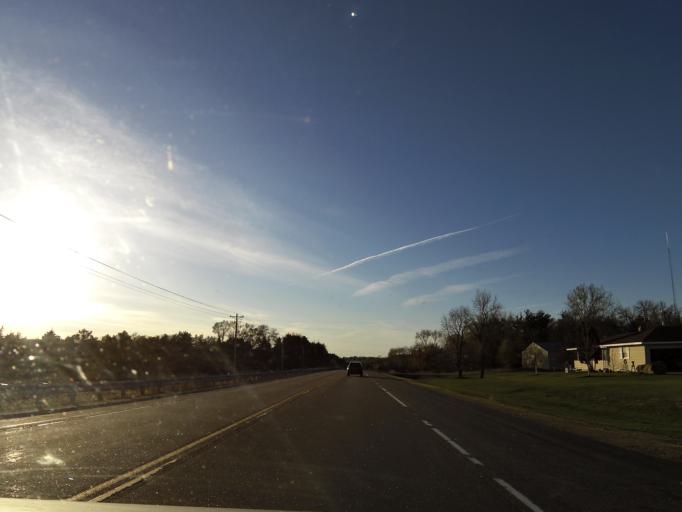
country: US
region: Wisconsin
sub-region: Pierce County
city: Prescott
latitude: 44.6934
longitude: -92.8177
